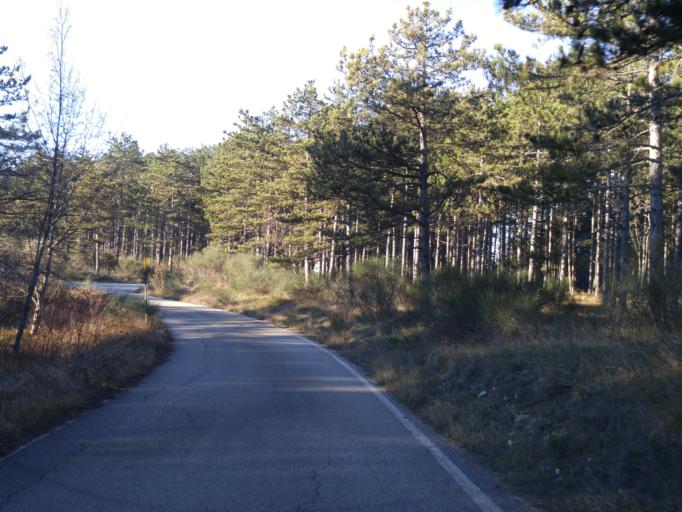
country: IT
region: The Marches
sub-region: Provincia di Pesaro e Urbino
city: Isola del Piano
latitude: 43.7064
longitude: 12.7571
